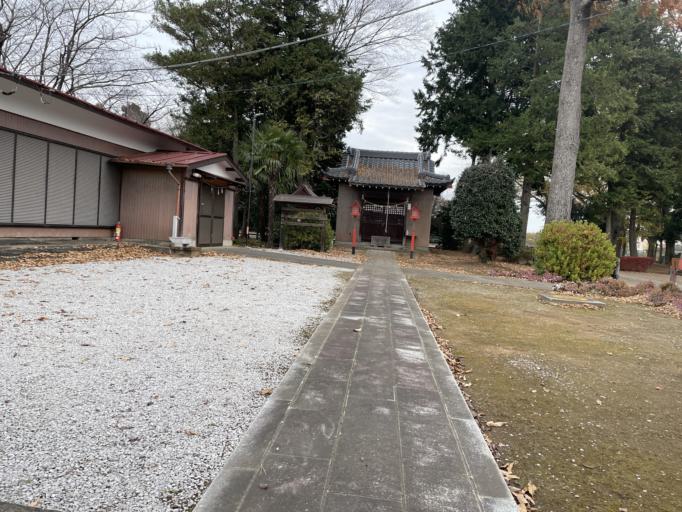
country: JP
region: Saitama
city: Shiraoka
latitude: 36.0285
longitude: 139.6407
